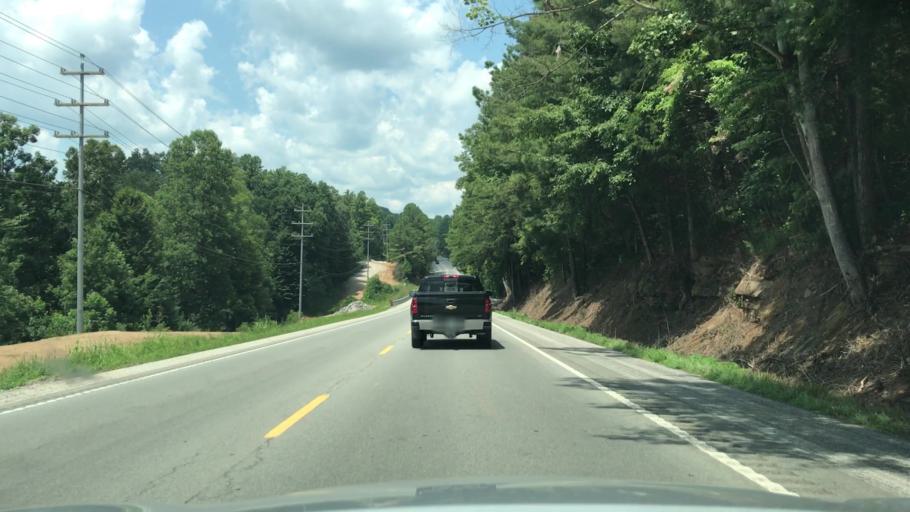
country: US
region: Tennessee
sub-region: Overton County
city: Livingston
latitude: 36.4399
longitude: -85.2567
